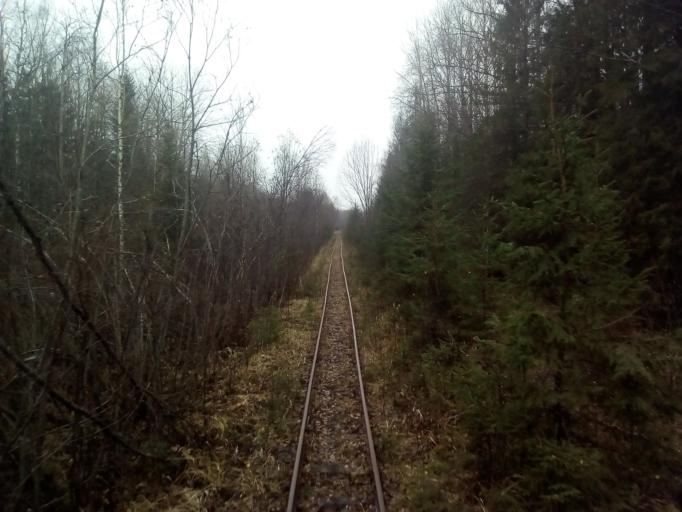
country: RU
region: Vologda
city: Kharovsk
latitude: 59.8102
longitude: 40.3799
